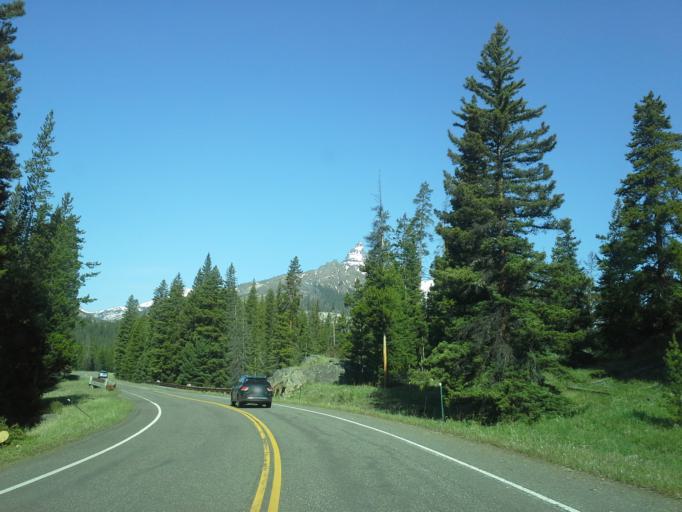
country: US
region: Montana
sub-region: Carbon County
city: Red Lodge
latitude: 44.9577
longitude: -109.8046
